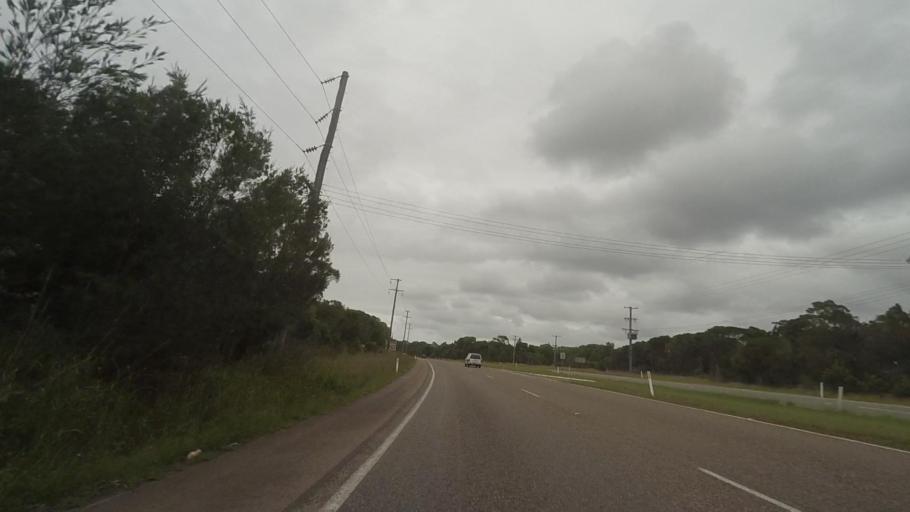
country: AU
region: New South Wales
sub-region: Wyong Shire
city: Kingfisher Shores
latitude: -33.1895
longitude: 151.5291
